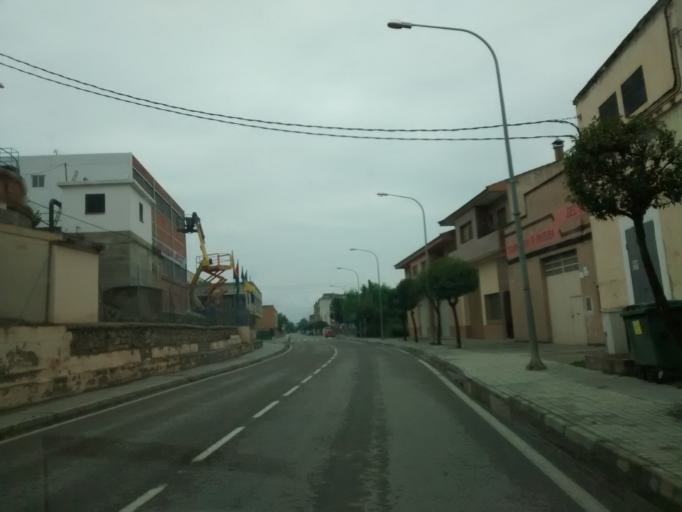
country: ES
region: Aragon
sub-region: Provincia de Zaragoza
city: Caspe
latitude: 41.2298
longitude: -0.0378
